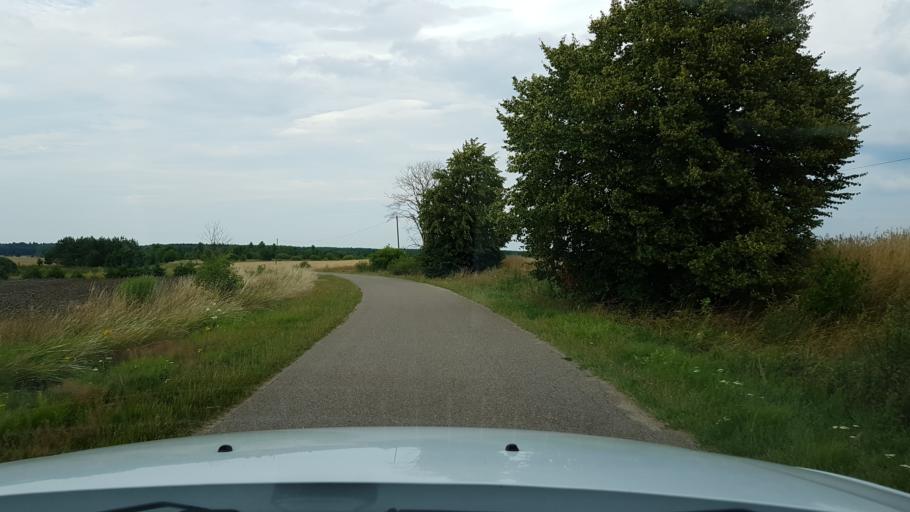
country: PL
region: West Pomeranian Voivodeship
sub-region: Powiat drawski
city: Wierzchowo
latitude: 53.4637
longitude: 16.1116
